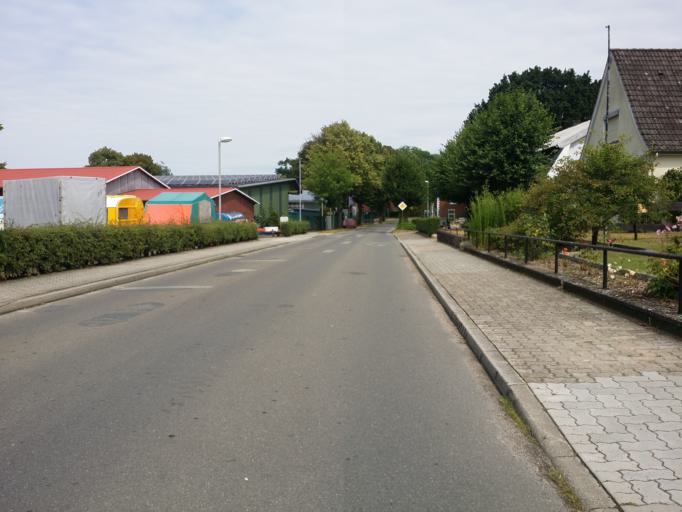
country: DE
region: Schleswig-Holstein
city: Vaale
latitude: 54.0003
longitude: 9.3799
